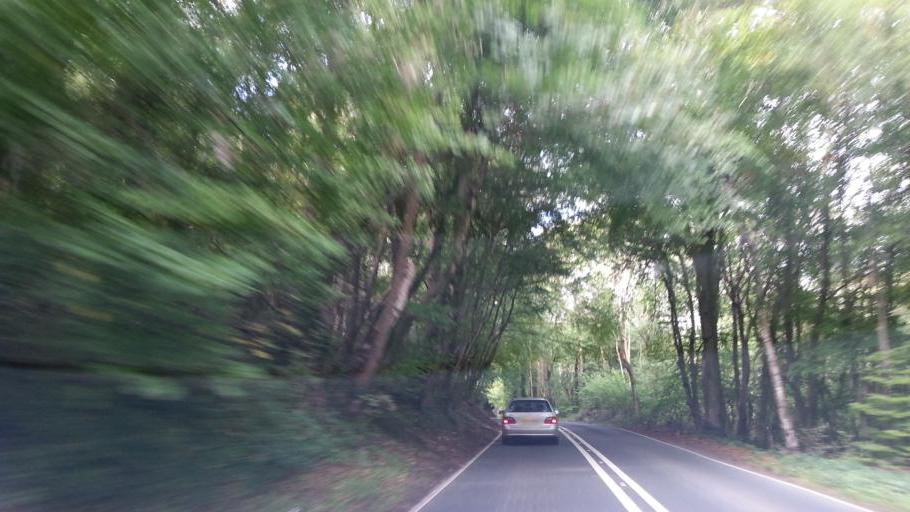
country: GB
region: England
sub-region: Gloucestershire
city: Painswick
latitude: 51.7987
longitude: -2.1901
